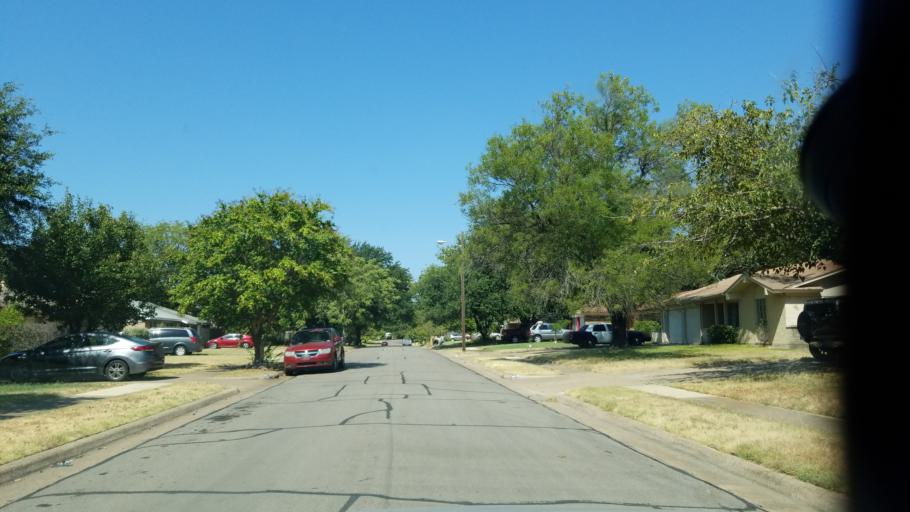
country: US
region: Texas
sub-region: Dallas County
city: Duncanville
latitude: 32.6413
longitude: -96.9017
